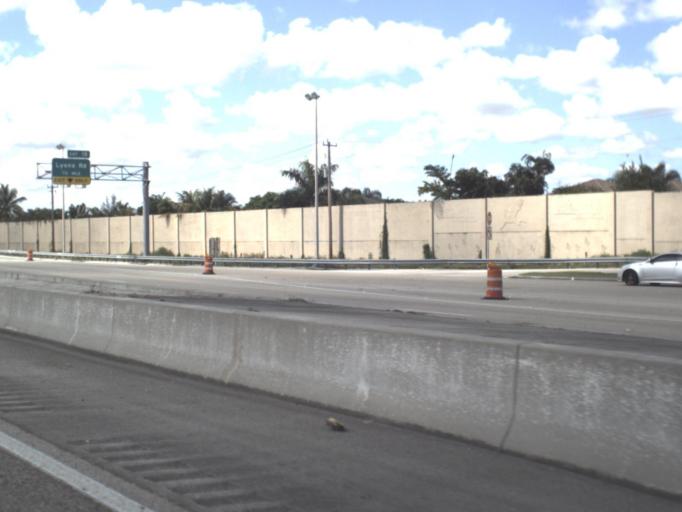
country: US
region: Florida
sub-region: Palm Beach County
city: Boca Pointe
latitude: 26.3055
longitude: -80.1745
